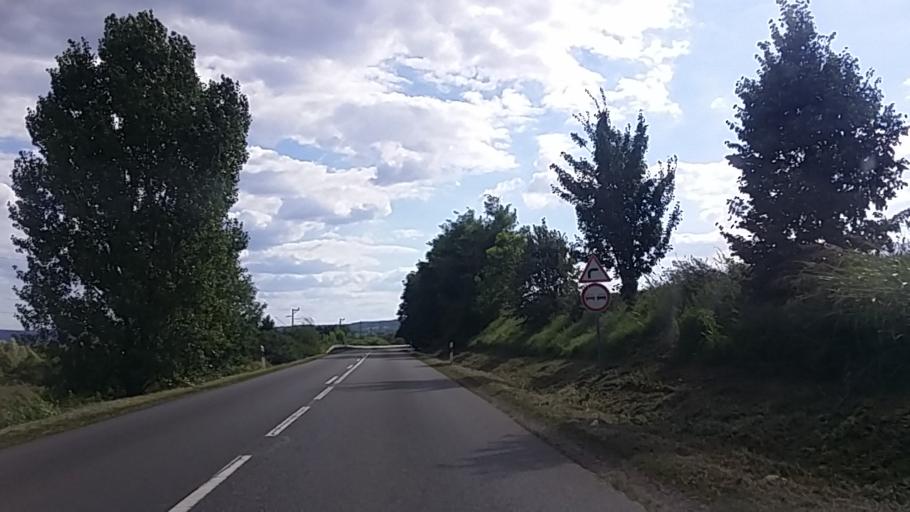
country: HU
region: Baranya
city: Sasd
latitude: 46.2873
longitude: 18.1190
